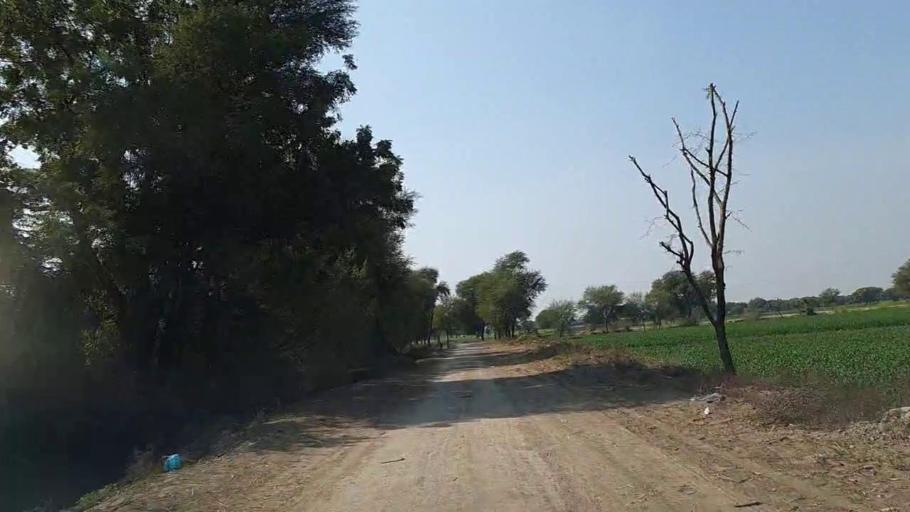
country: PK
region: Sindh
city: Nawabshah
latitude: 26.2471
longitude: 68.4750
